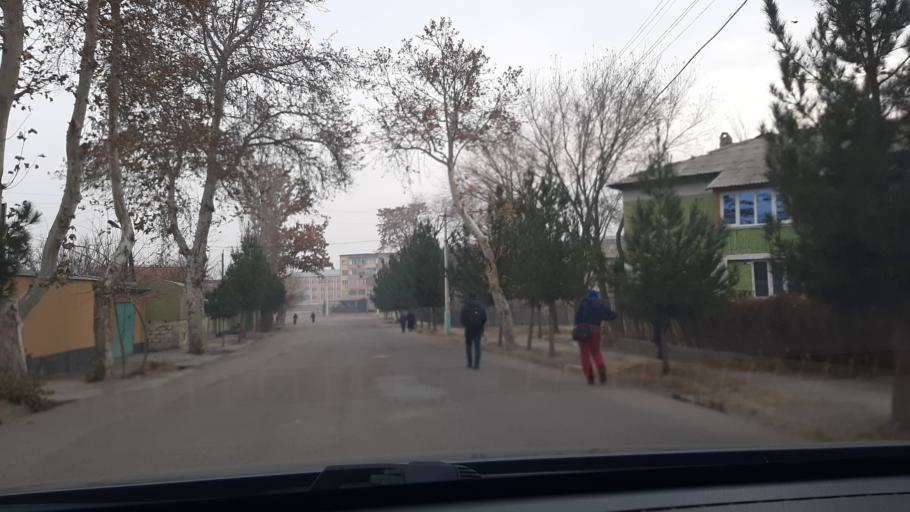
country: TJ
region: Viloyati Sughd
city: Palos
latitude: 40.2626
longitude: 69.7907
